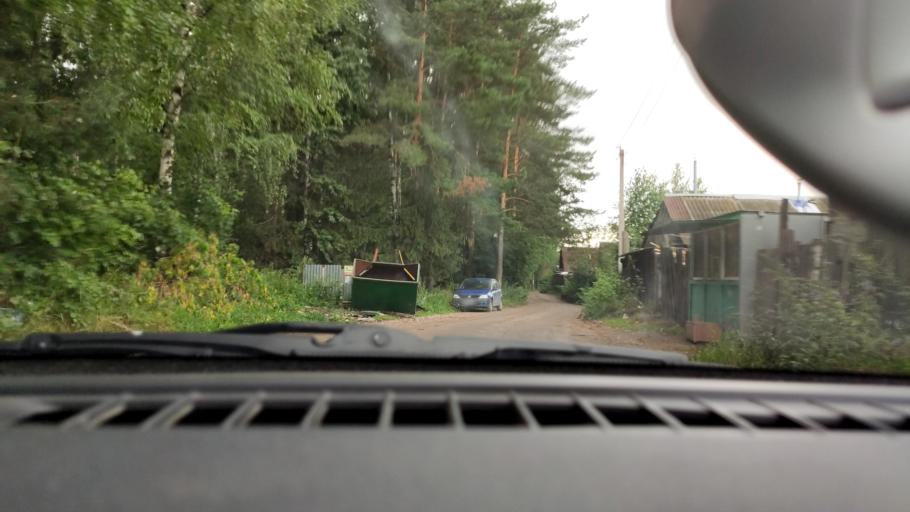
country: RU
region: Perm
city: Overyata
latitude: 58.0524
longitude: 55.9827
